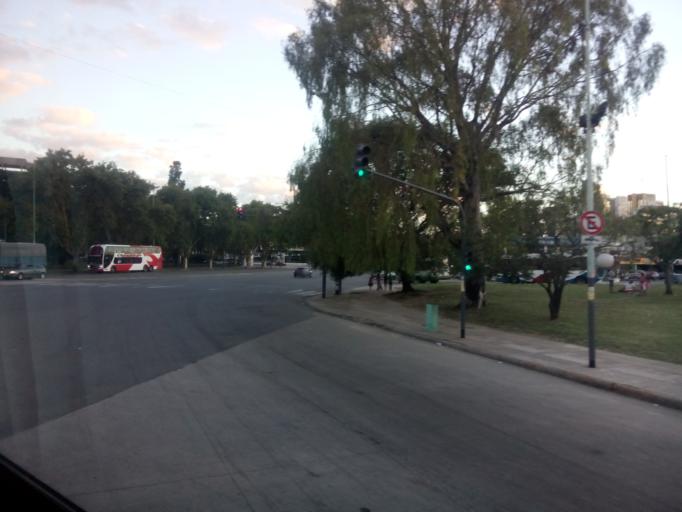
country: AR
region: Buenos Aires F.D.
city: Retiro
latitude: -34.5857
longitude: -58.3728
